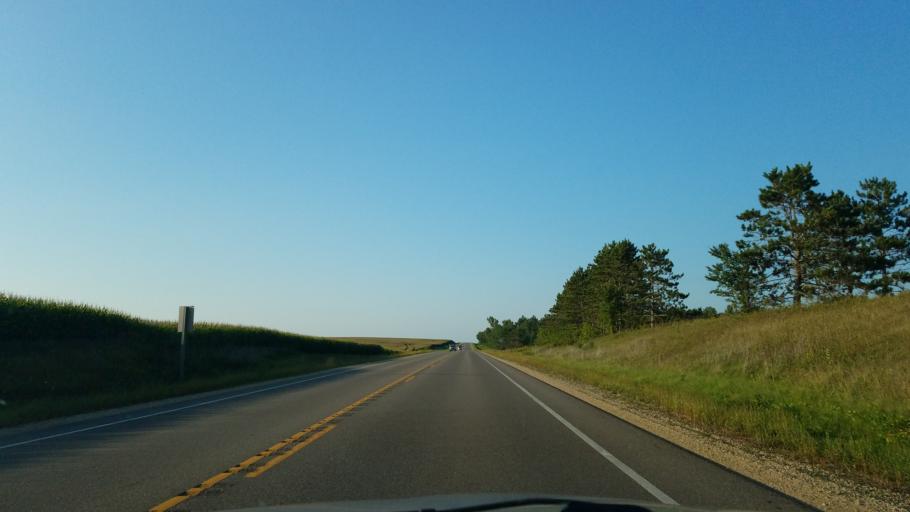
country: US
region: Wisconsin
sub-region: Saint Croix County
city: Baldwin
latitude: 45.0807
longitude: -92.3753
